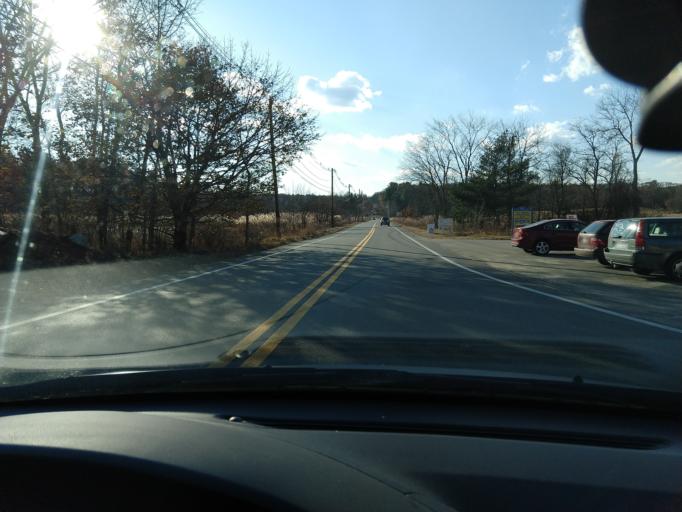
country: US
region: Massachusetts
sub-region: Middlesex County
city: Littleton Common
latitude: 42.5532
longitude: -71.4526
